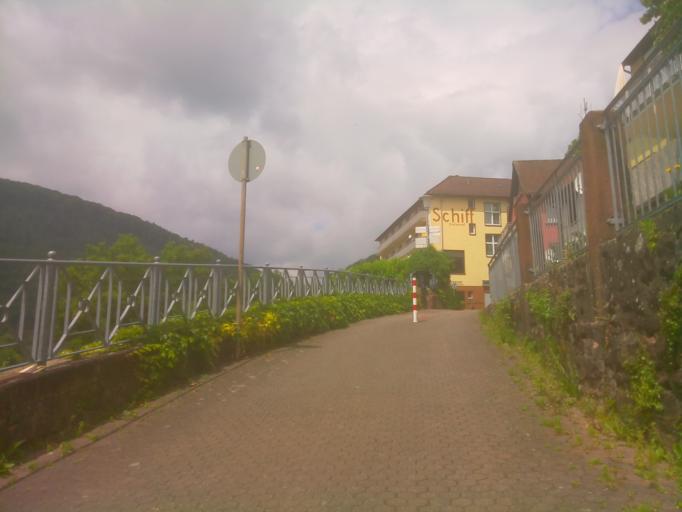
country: DE
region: Hesse
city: Neckarsteinach
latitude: 49.4075
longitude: 8.8360
